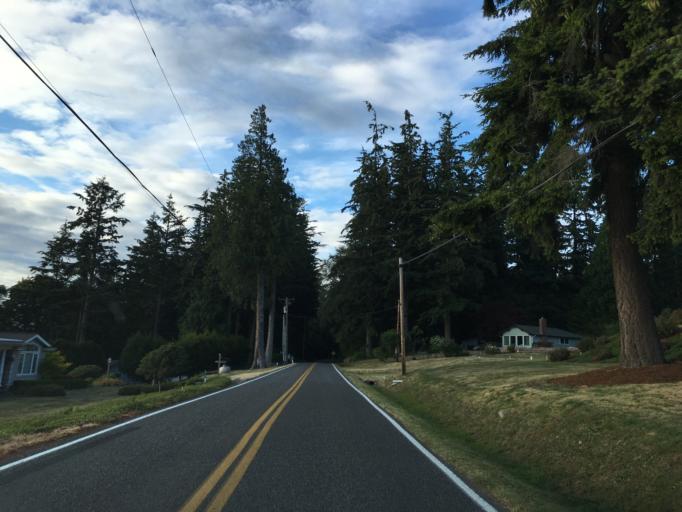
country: CA
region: British Columbia
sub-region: Greater Vancouver Regional District
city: White Rock
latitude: 48.9657
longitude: -122.8019
